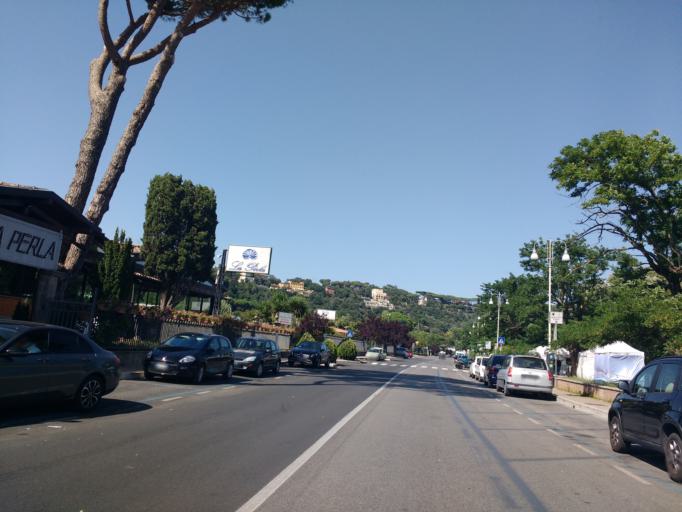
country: IT
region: Latium
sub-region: Citta metropolitana di Roma Capitale
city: Castel Gandolfo
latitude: 41.7574
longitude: 12.6529
